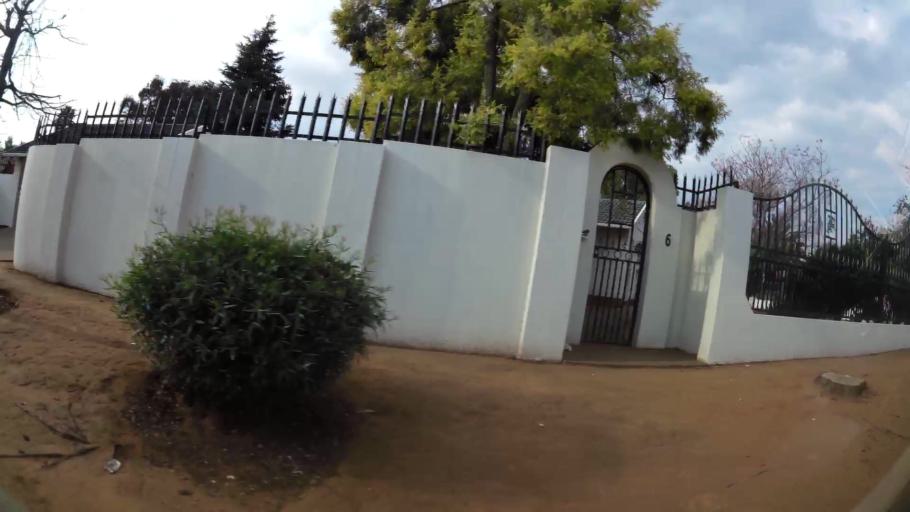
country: ZA
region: Gauteng
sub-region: Ekurhuleni Metropolitan Municipality
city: Benoni
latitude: -26.1186
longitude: 28.3712
